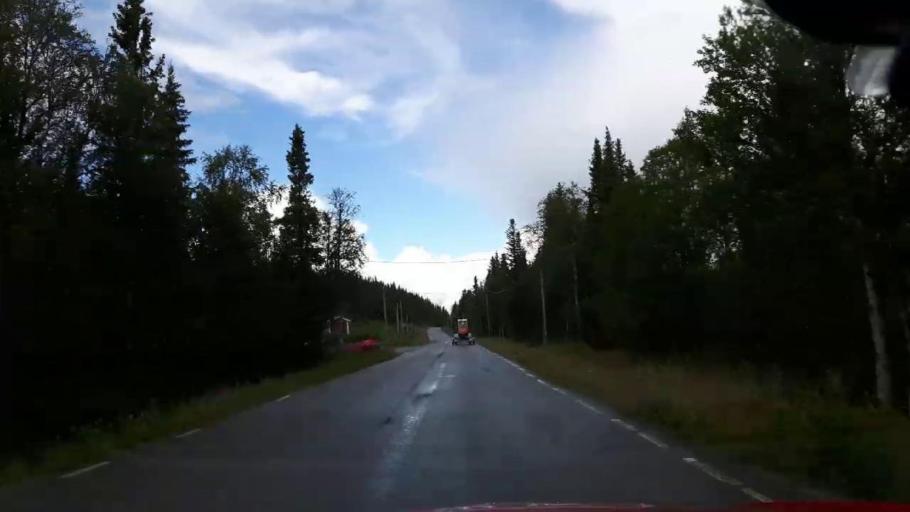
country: SE
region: Vaesterbotten
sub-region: Vilhelmina Kommun
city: Sjoberg
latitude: 64.9738
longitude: 15.3297
